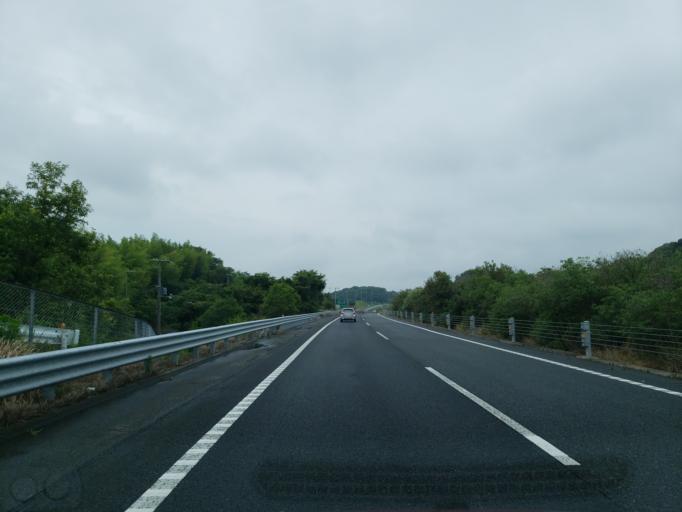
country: JP
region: Hyogo
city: Sumoto
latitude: 34.4529
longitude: 134.8780
